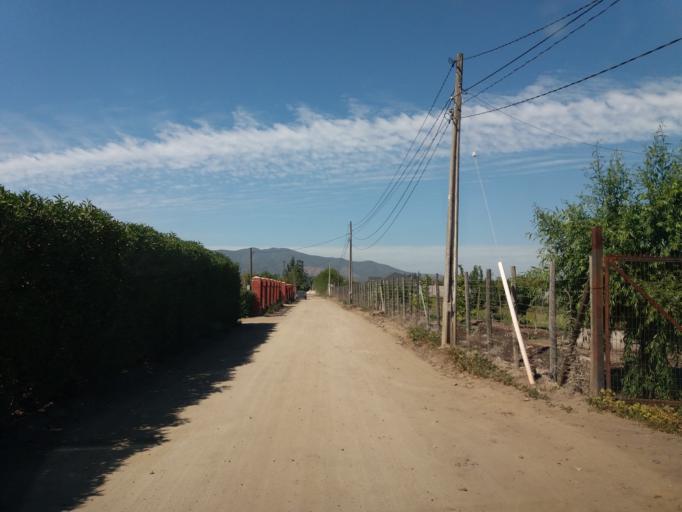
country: CL
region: Valparaiso
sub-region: Provincia de Quillota
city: Quillota
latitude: -32.8693
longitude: -71.2237
